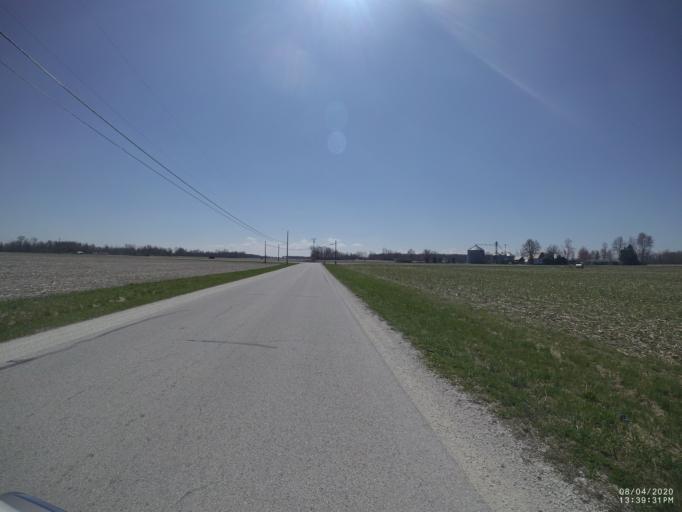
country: US
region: Ohio
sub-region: Sandusky County
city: Gibsonburg
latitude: 41.3276
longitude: -83.2918
